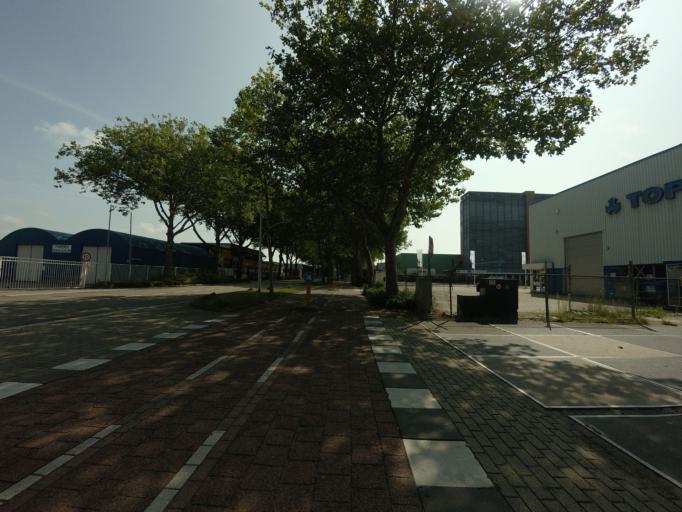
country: NL
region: South Holland
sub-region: Gemeente Papendrecht
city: Papendrecht
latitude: 51.8283
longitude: 4.7245
